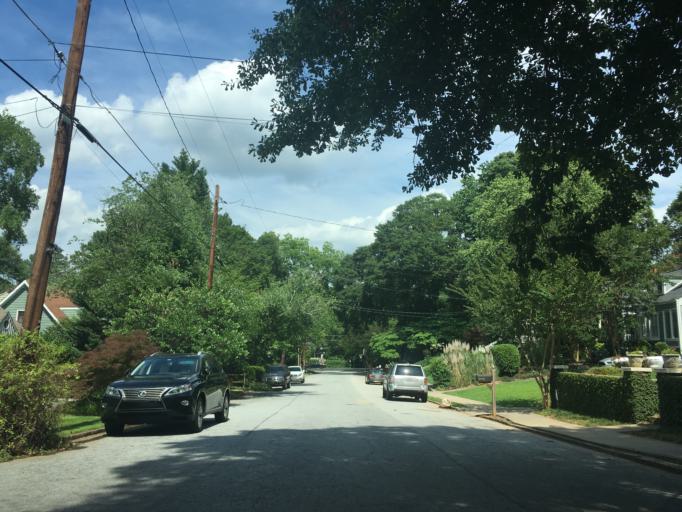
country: US
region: Georgia
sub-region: DeKalb County
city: Druid Hills
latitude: 33.7778
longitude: -84.3602
